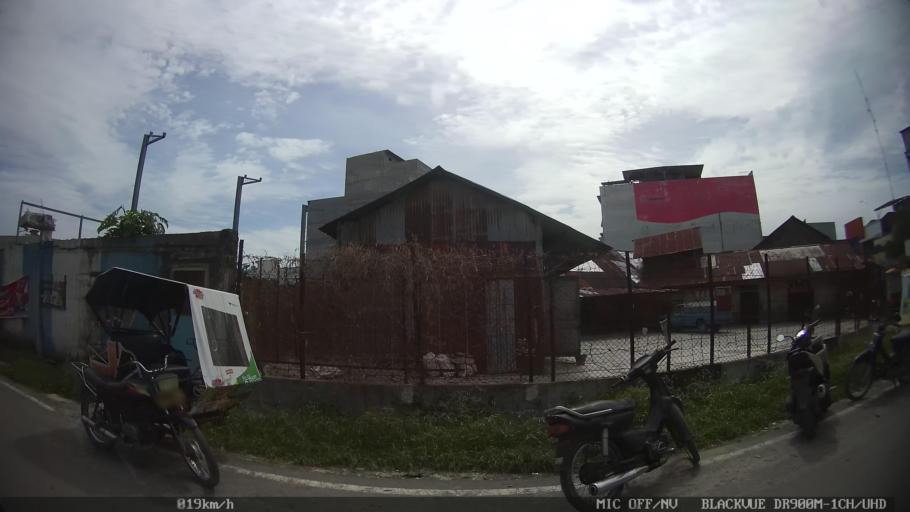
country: ID
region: North Sumatra
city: Percut
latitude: 3.6135
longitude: 98.8005
